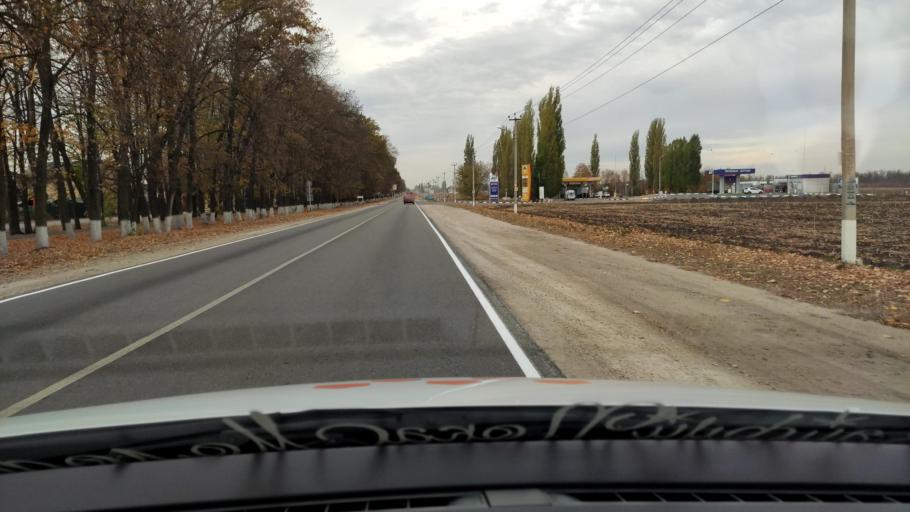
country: RU
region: Voronezj
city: Ramon'
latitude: 51.9120
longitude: 39.3248
